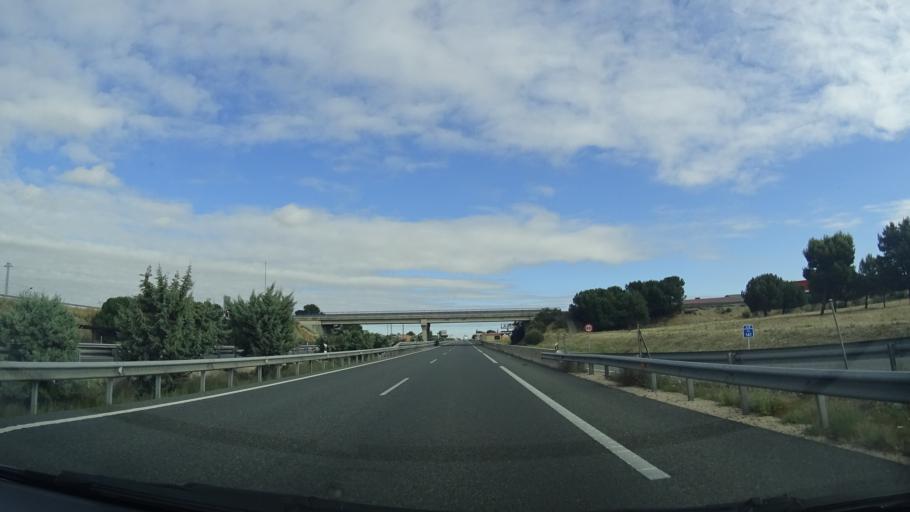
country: ES
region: Castille and Leon
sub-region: Provincia de Valladolid
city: Ataquines
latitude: 41.1763
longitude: -4.8049
